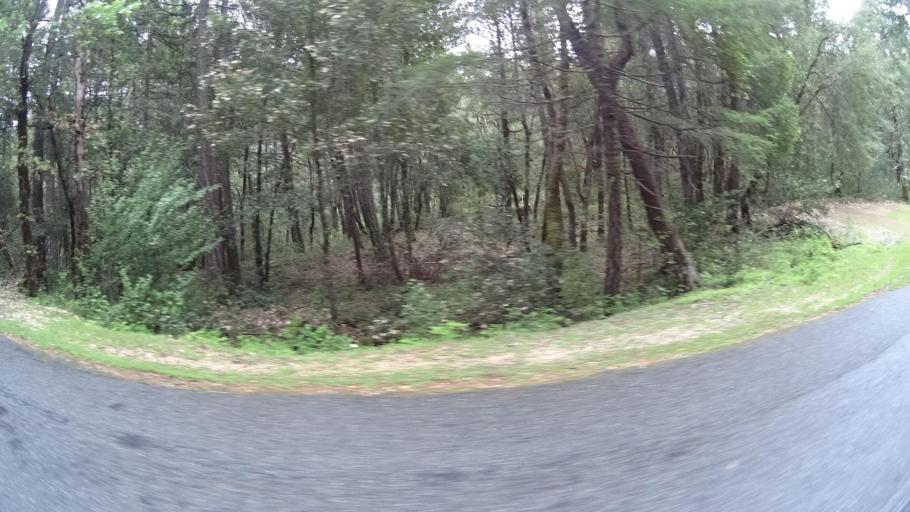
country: US
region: California
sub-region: Humboldt County
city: Willow Creek
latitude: 41.3488
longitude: -123.5124
